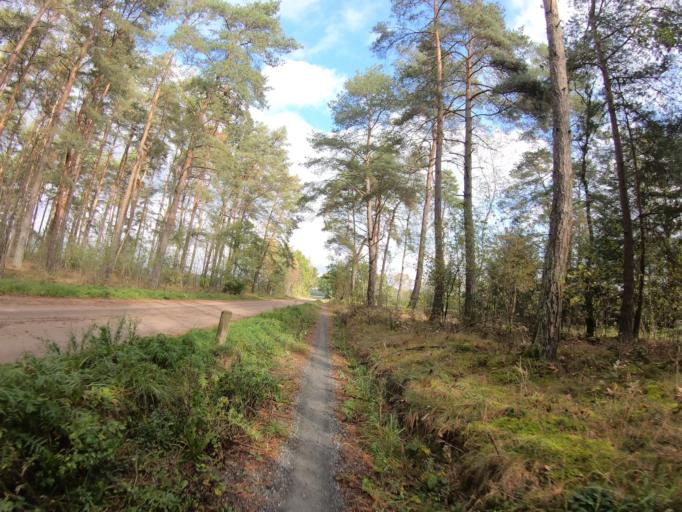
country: DE
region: Lower Saxony
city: Wesendorf
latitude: 52.5799
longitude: 10.5708
